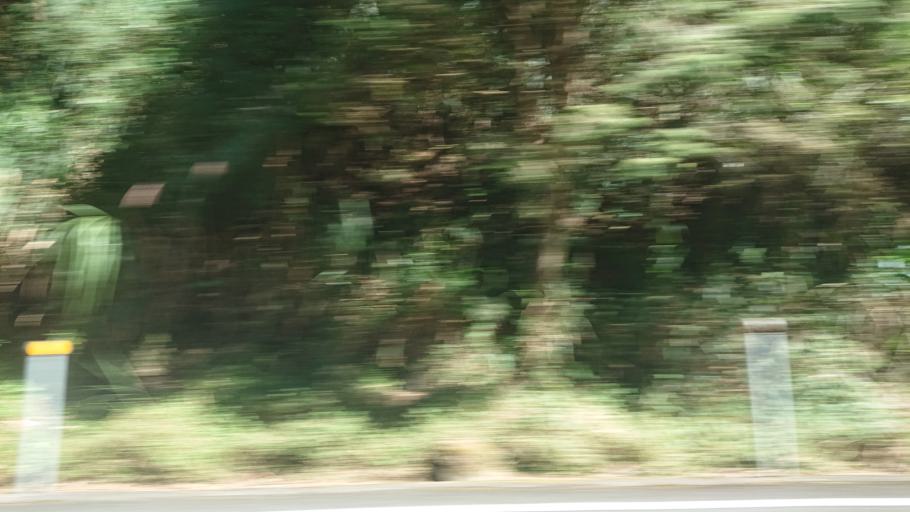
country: TW
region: Taiwan
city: Lugu
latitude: 23.5025
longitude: 120.7992
